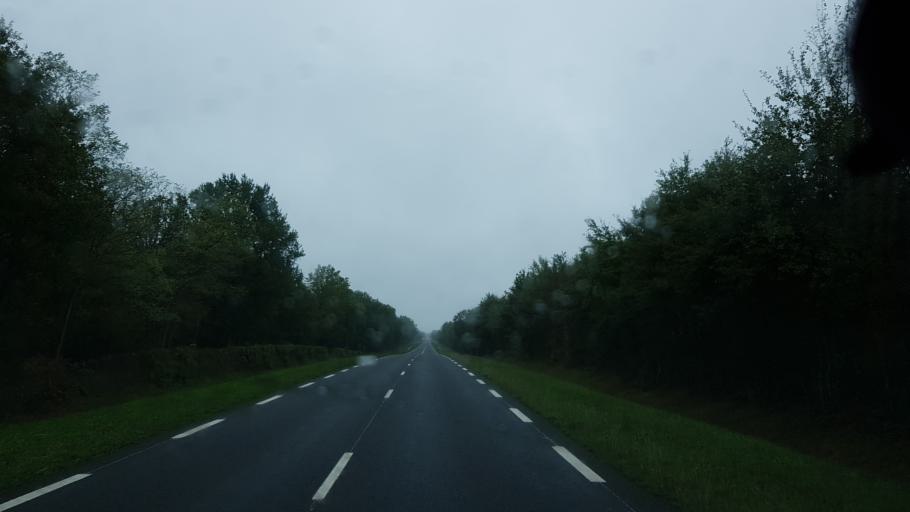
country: FR
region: Centre
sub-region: Departement du Loir-et-Cher
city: Salbris
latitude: 47.4752
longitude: 2.0404
